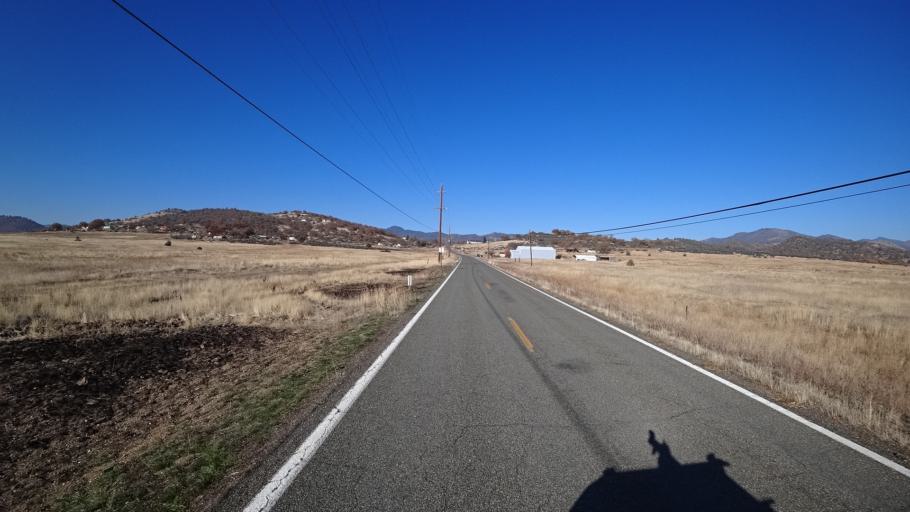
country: US
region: California
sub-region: Siskiyou County
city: Yreka
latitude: 41.7365
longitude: -122.5981
